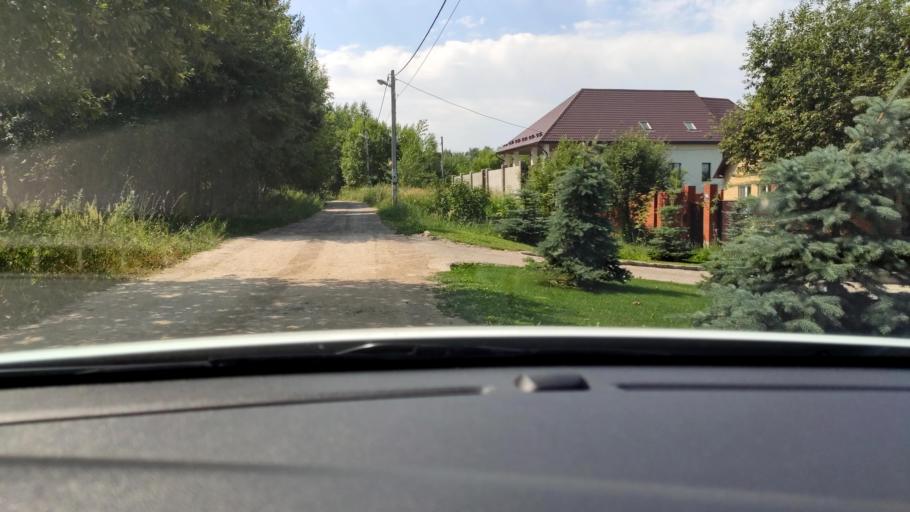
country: RU
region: Tatarstan
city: Stolbishchi
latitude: 55.7431
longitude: 49.2516
